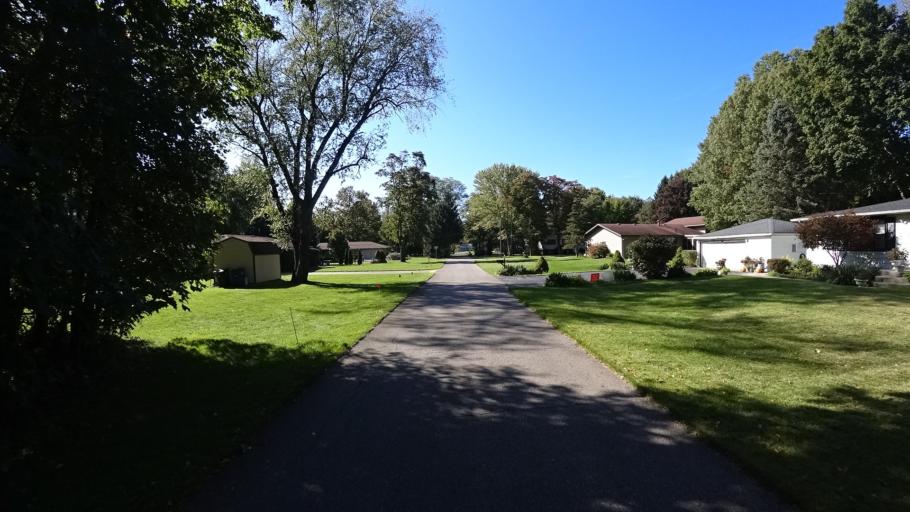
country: US
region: Indiana
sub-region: LaPorte County
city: Trail Creek
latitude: 41.7072
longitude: -86.8324
